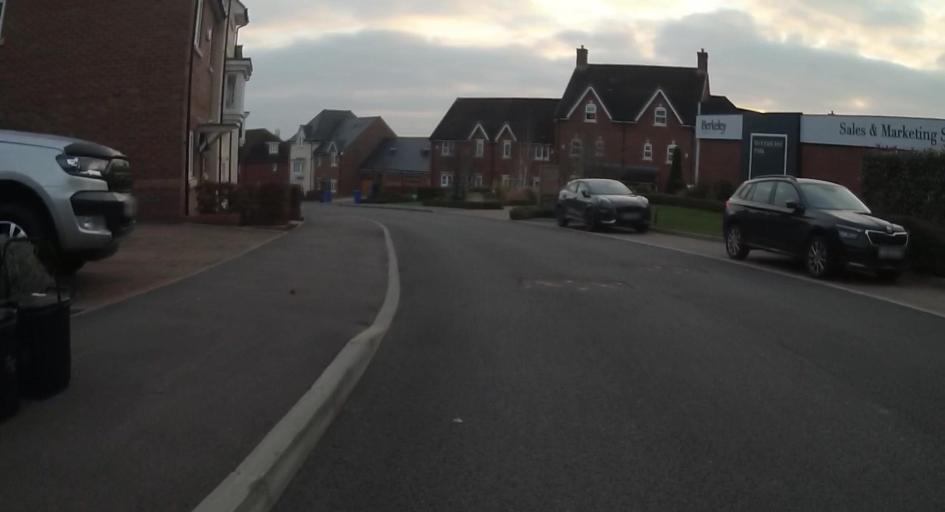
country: GB
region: England
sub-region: Bracknell Forest
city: Bracknell
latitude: 51.4286
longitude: -0.7621
